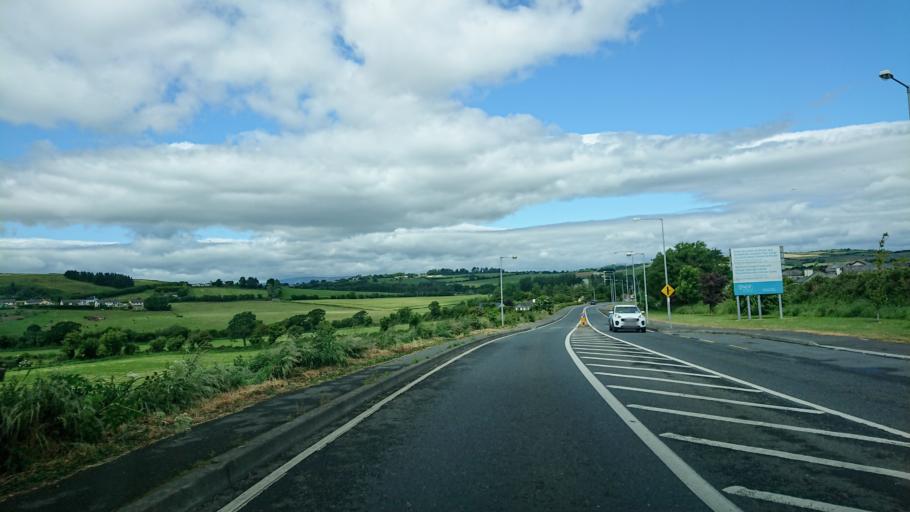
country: IE
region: Leinster
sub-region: Kilkenny
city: Mooncoin
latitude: 52.2274
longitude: -7.2336
